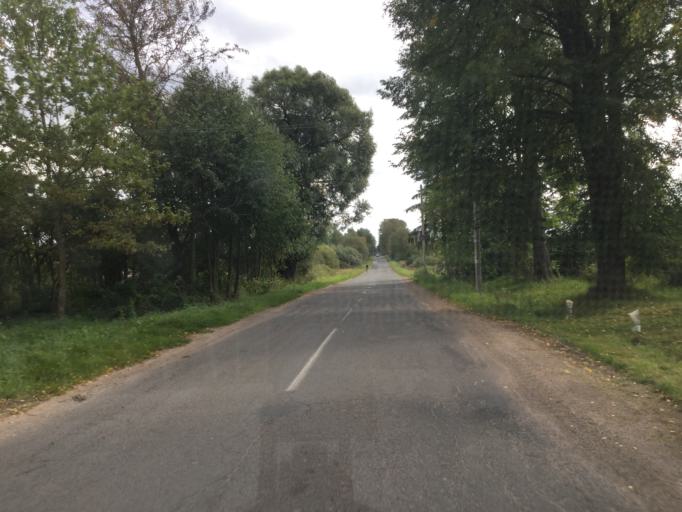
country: BY
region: Vitebsk
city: Vitebsk
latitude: 55.1483
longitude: 30.2794
